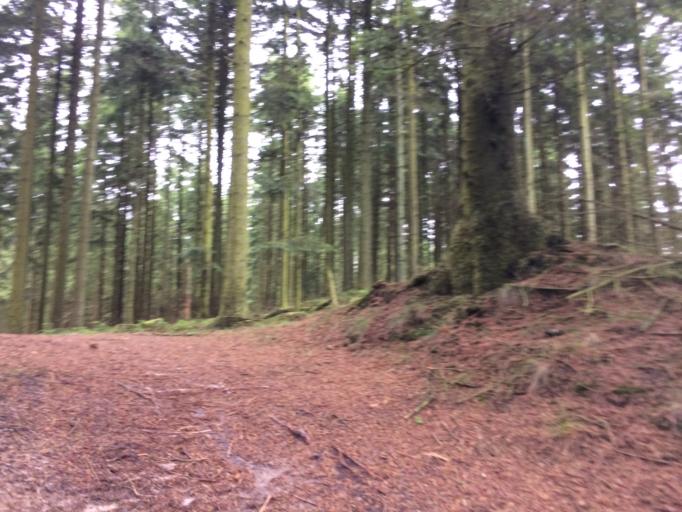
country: DK
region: Central Jutland
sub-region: Holstebro Kommune
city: Ulfborg
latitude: 56.2487
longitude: 8.4474
